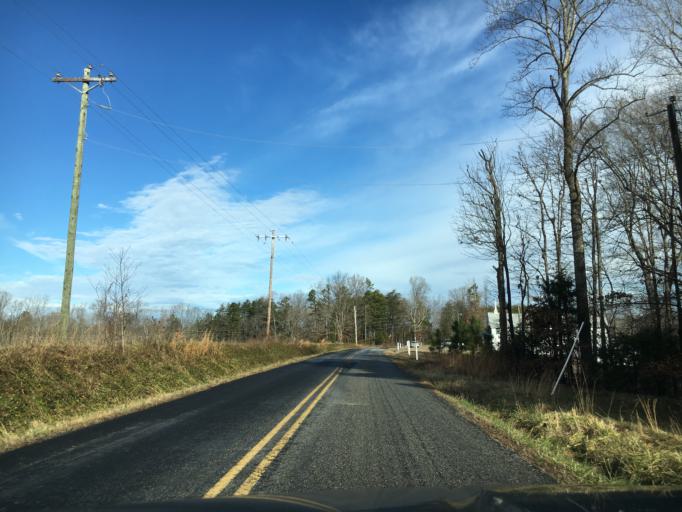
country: US
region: Virginia
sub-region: Nottoway County
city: Crewe
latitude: 37.3054
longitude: -78.1951
